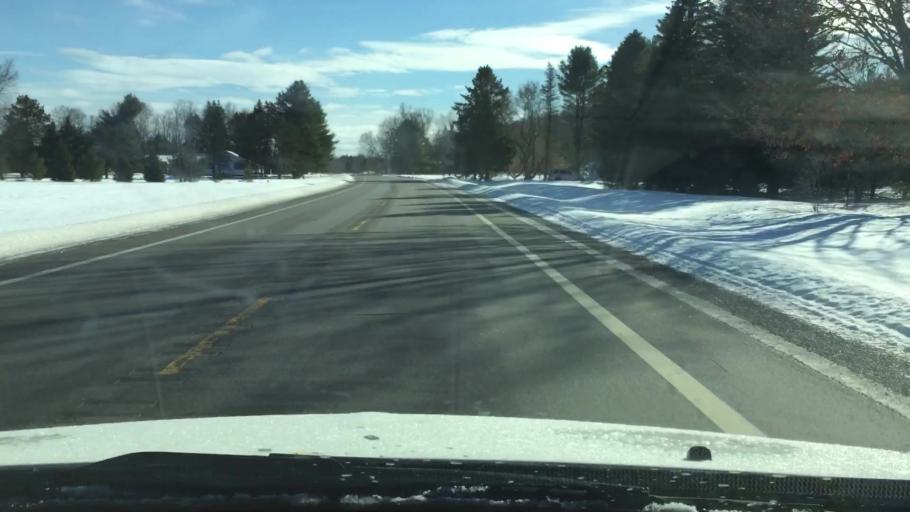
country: US
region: Michigan
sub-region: Charlevoix County
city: East Jordan
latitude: 45.0683
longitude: -85.0844
